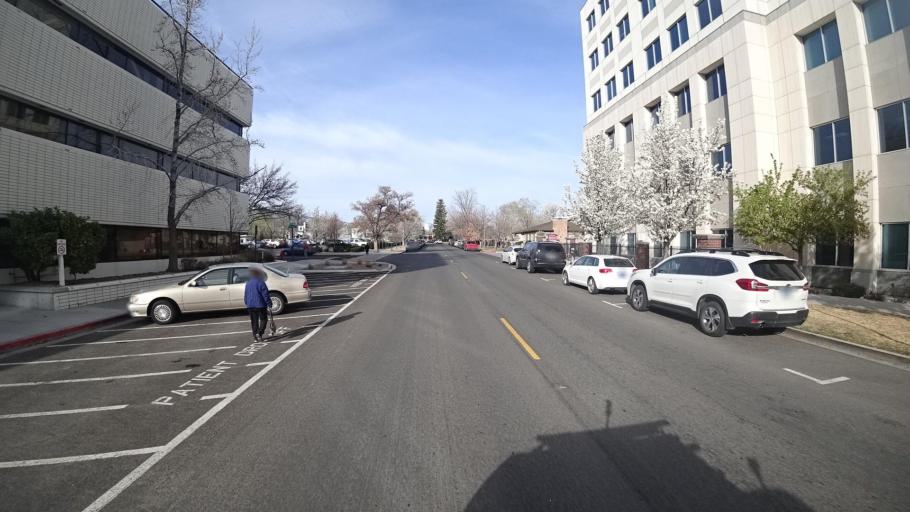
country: US
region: Nevada
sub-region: Washoe County
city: Reno
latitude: 39.5313
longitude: -119.8198
